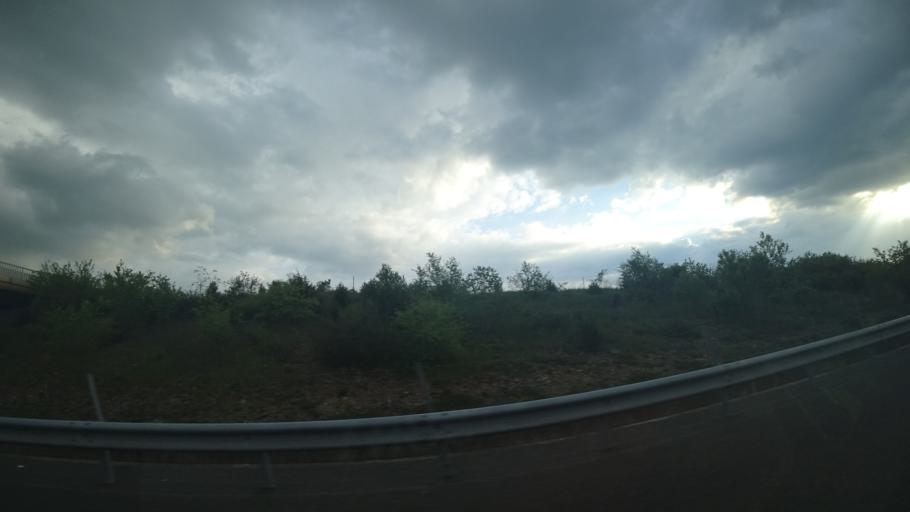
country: FR
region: Midi-Pyrenees
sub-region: Departement de l'Aveyron
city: La Cavalerie
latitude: 44.0172
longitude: 3.1327
